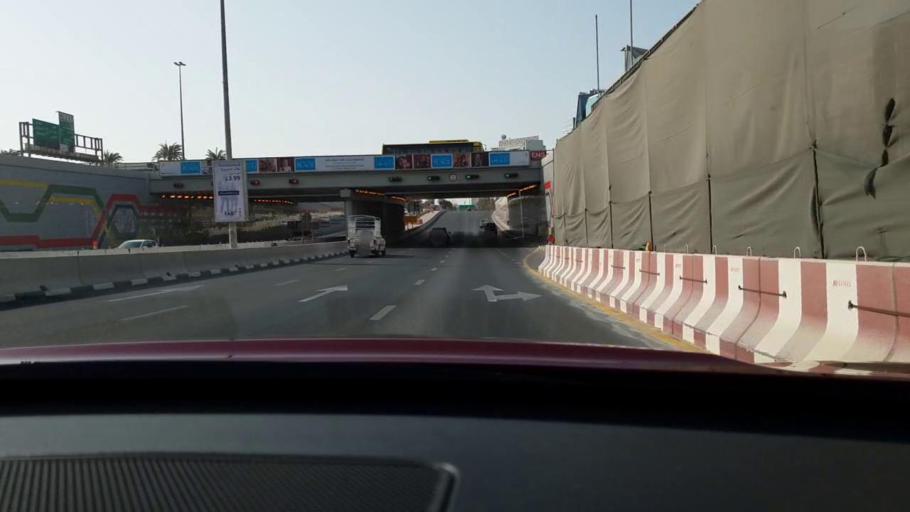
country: AE
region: Ash Shariqah
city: Sharjah
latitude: 25.2549
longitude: 55.3249
